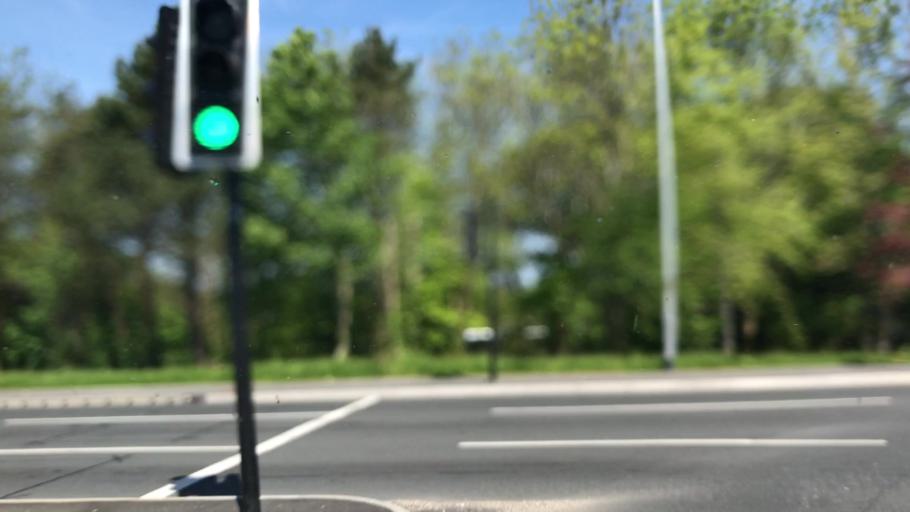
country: GB
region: England
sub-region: Cornwall
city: Chacewater
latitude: 50.2643
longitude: -5.1195
